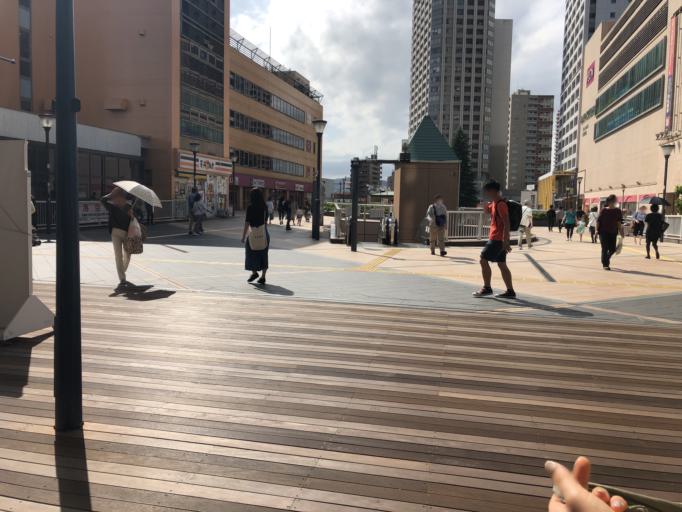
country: JP
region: Tokyo
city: Hachioji
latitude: 35.5954
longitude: 139.3451
